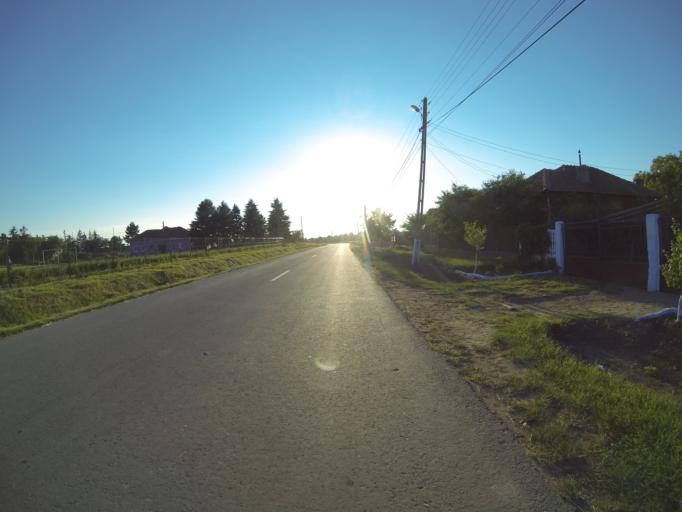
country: RO
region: Dolj
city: Satu Nou Calopar
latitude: 44.1618
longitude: 23.7707
